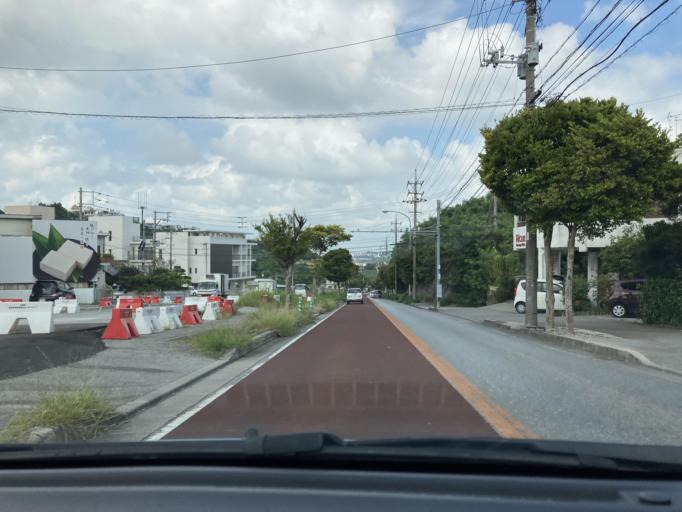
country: JP
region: Okinawa
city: Ginowan
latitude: 26.2261
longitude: 127.7359
